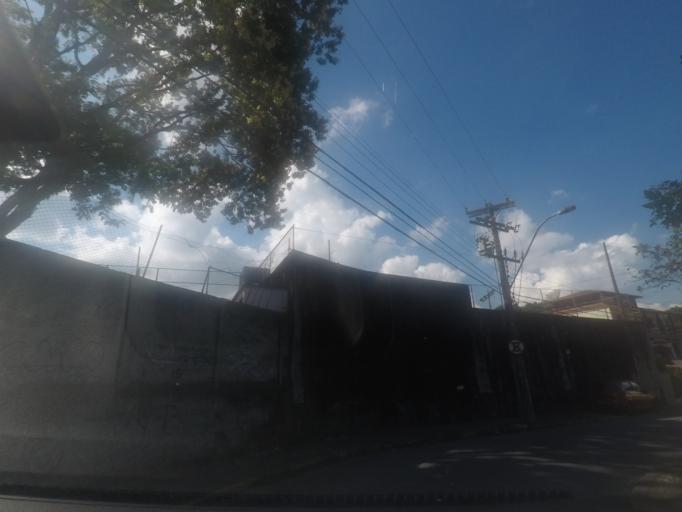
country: BR
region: Rio de Janeiro
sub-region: Petropolis
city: Petropolis
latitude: -22.5198
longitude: -43.1923
